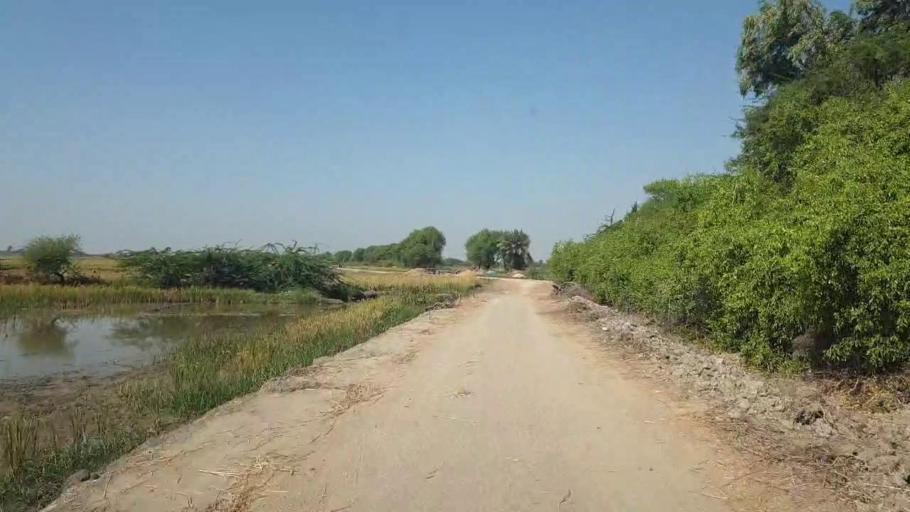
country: PK
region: Sindh
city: Talhar
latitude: 24.8042
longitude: 68.8090
